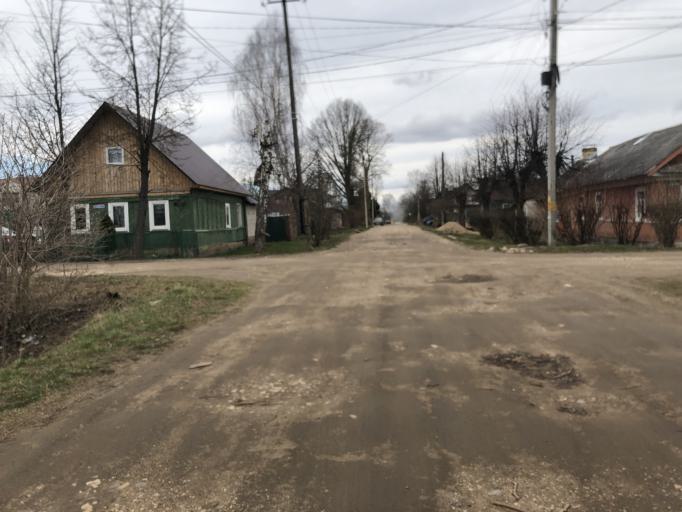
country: RU
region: Tverskaya
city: Rzhev
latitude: 56.2513
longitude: 34.3170
